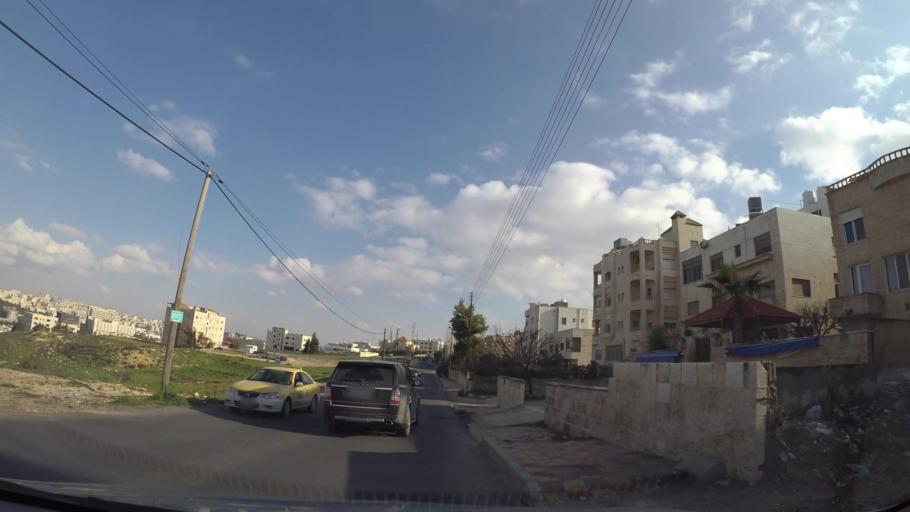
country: JO
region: Amman
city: Al Jubayhah
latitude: 32.0091
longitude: 35.8646
